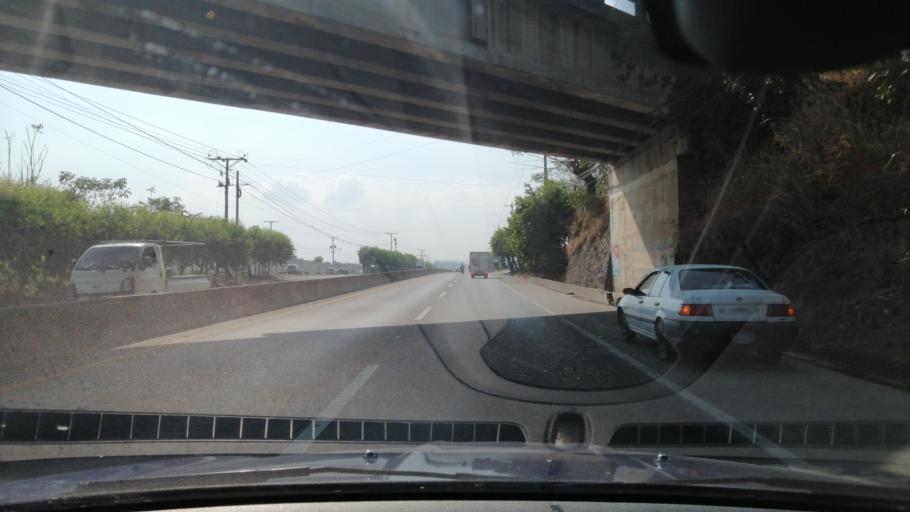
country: SV
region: San Salvador
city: Apopa
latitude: 13.7973
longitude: -89.2290
